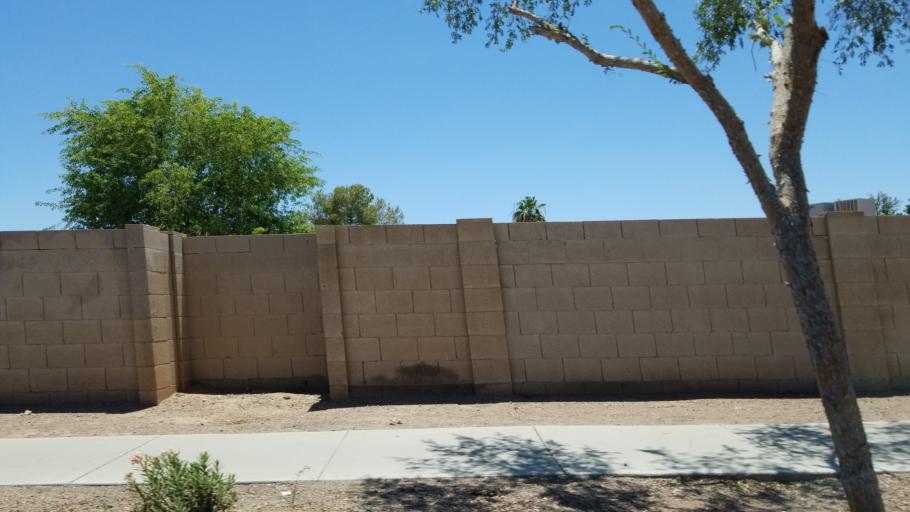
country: US
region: Arizona
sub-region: Maricopa County
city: Tolleson
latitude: 33.5087
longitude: -112.2479
